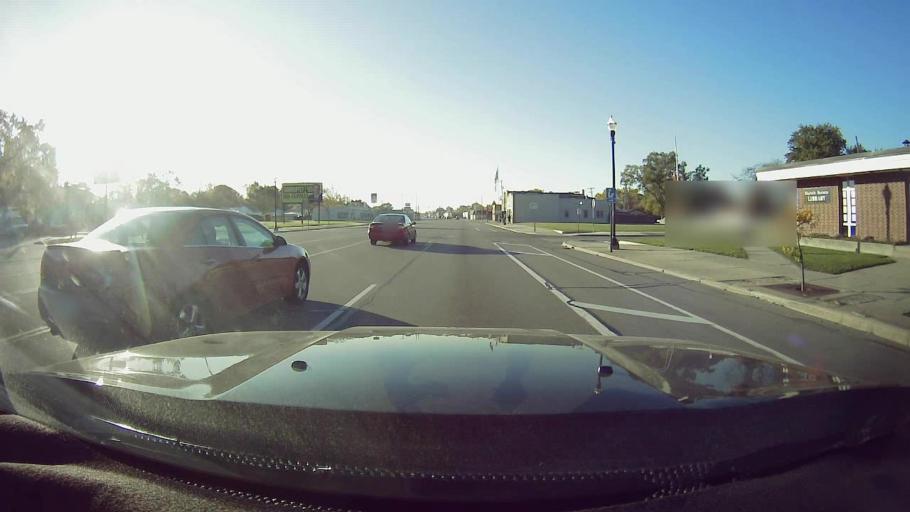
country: US
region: Michigan
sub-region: Macomb County
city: Warren
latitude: 42.4577
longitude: -83.0265
